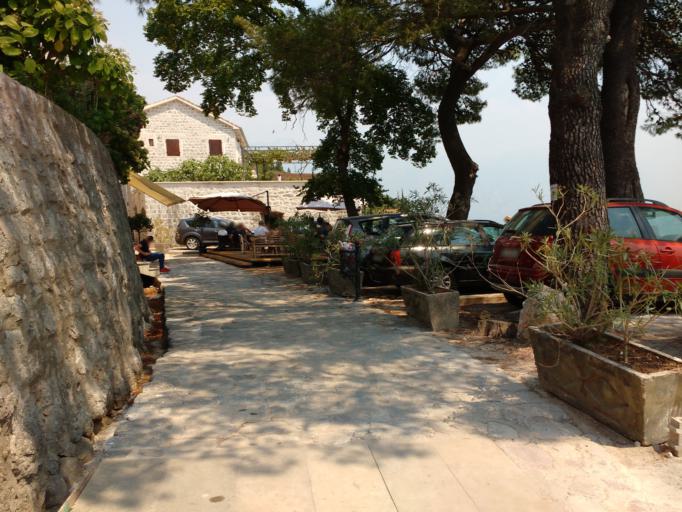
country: ME
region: Kotor
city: Risan
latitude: 42.4851
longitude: 18.7012
